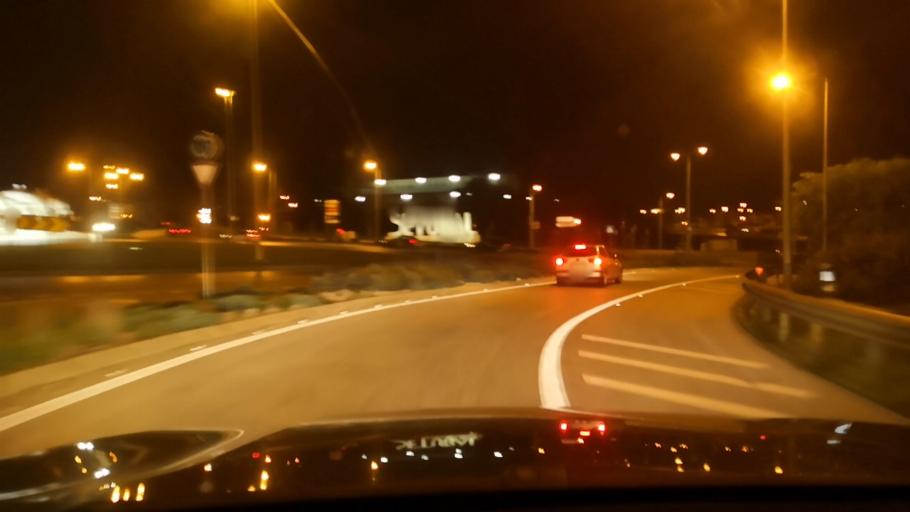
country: PT
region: Setubal
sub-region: Setubal
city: Setubal
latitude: 38.5365
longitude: -8.8745
